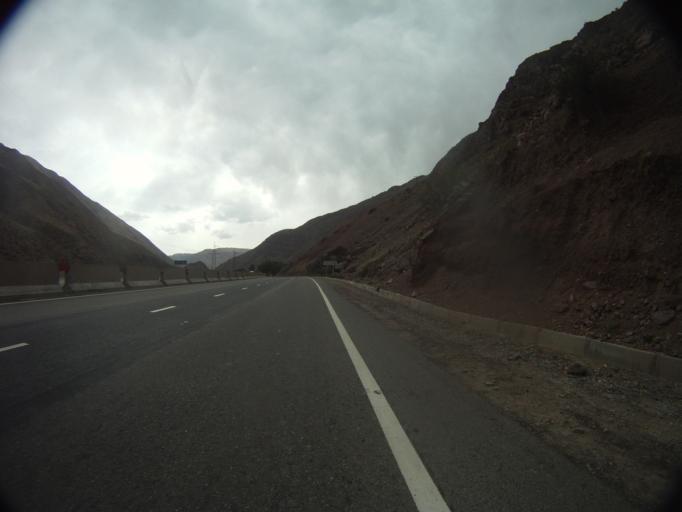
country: KG
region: Chuy
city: Bystrovka
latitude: 42.6467
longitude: 75.8686
